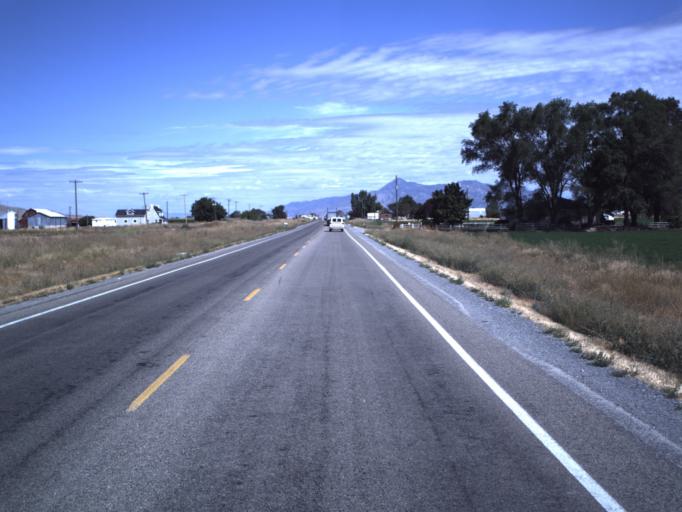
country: US
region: Utah
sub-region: Box Elder County
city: Elwood
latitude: 41.7014
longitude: -112.1419
